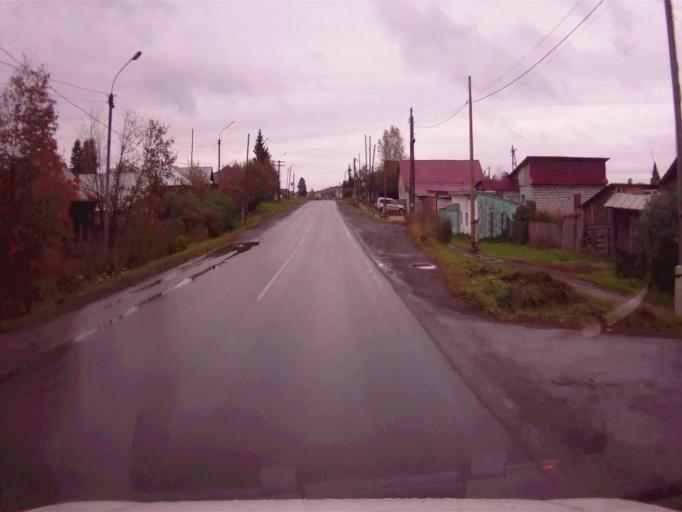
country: RU
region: Chelyabinsk
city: Verkhniy Ufaley
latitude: 56.0543
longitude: 60.2044
